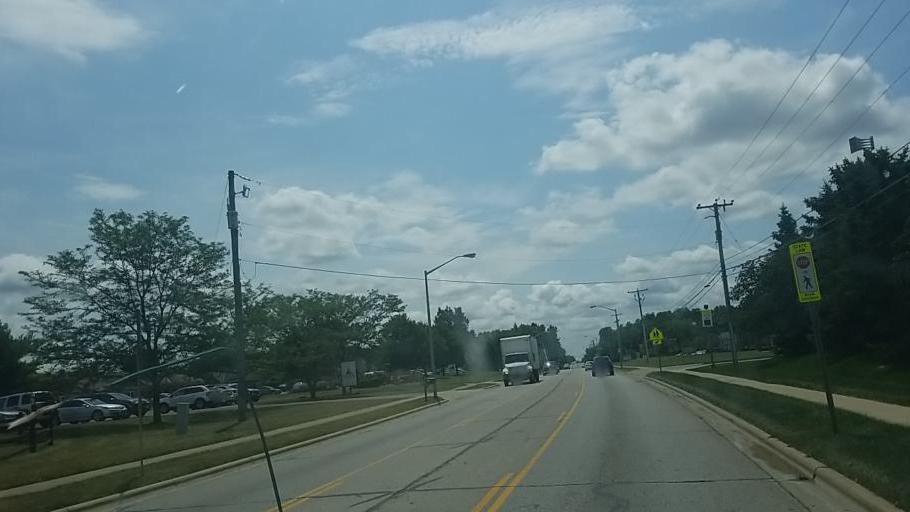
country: US
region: Ohio
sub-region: Franklin County
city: Reynoldsburg
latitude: 39.9721
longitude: -82.7702
